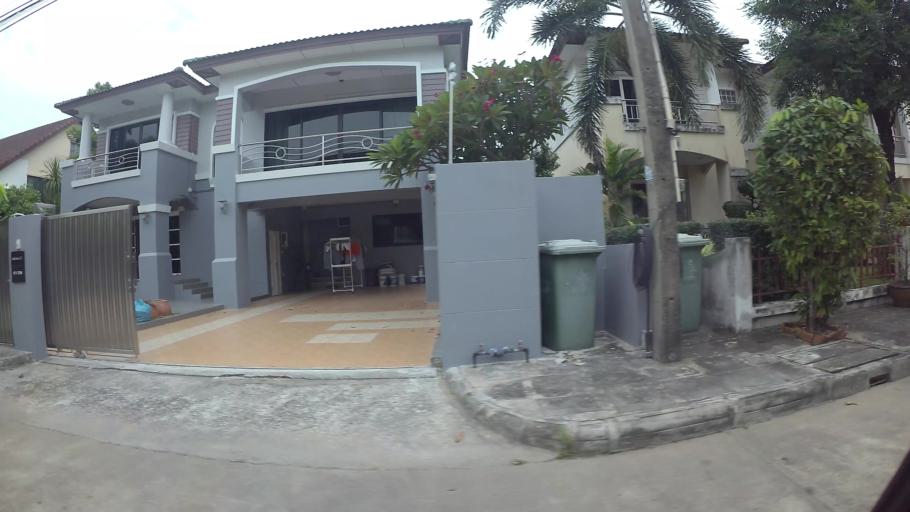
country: TH
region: Chon Buri
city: Si Racha
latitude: 13.1514
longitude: 100.9812
